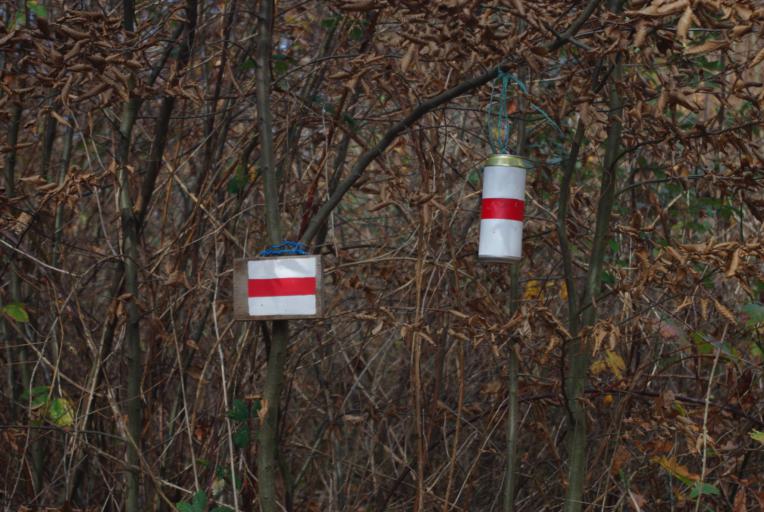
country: HU
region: Borsod-Abauj-Zemplen
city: Sarospatak
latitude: 48.3899
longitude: 21.5636
